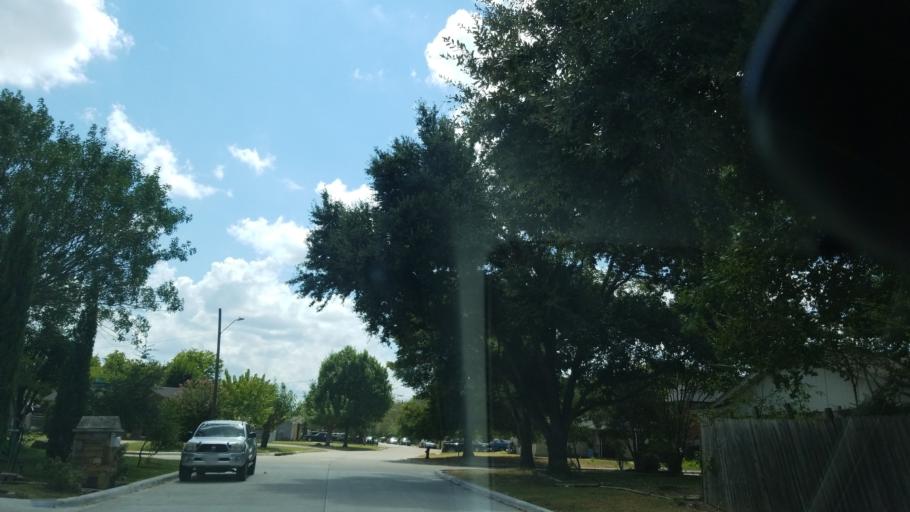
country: US
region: Texas
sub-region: Dallas County
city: Grand Prairie
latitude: 32.7173
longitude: -96.9831
